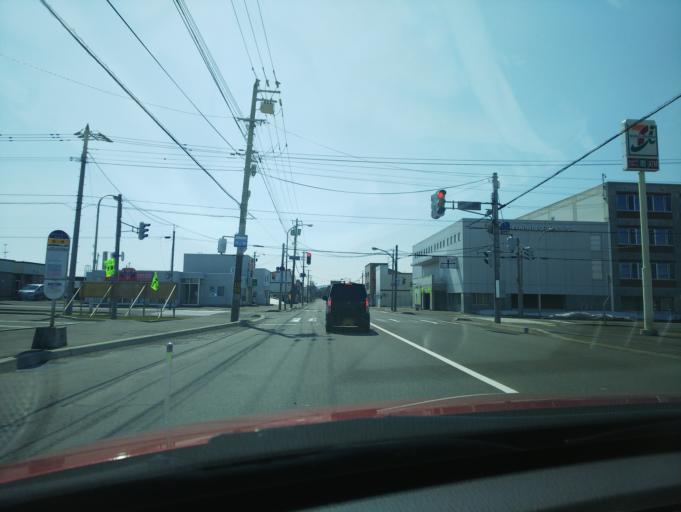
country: JP
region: Hokkaido
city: Nayoro
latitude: 44.2931
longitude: 142.4205
